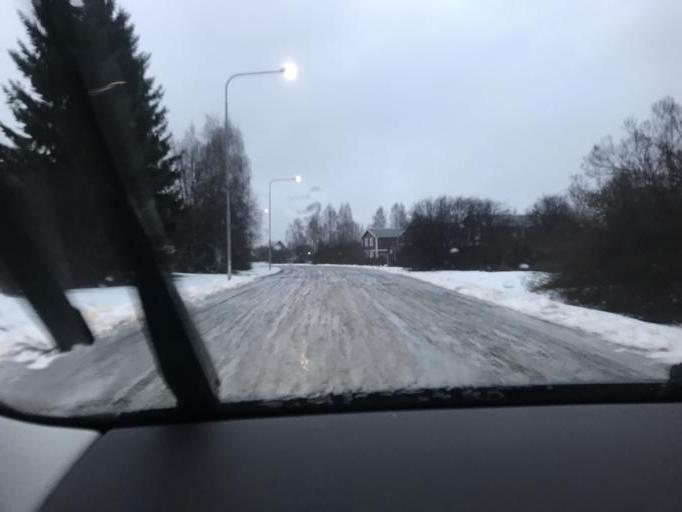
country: SE
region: Norrbotten
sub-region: Lulea Kommun
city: Sodra Sunderbyn
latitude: 65.6497
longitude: 21.9633
